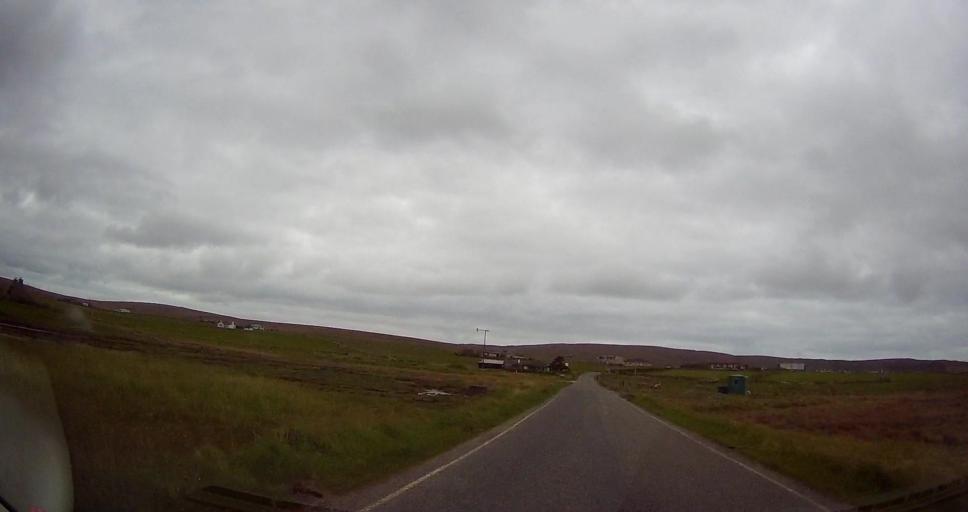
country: GB
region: Scotland
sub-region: Shetland Islands
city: Shetland
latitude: 60.7578
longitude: -0.8637
